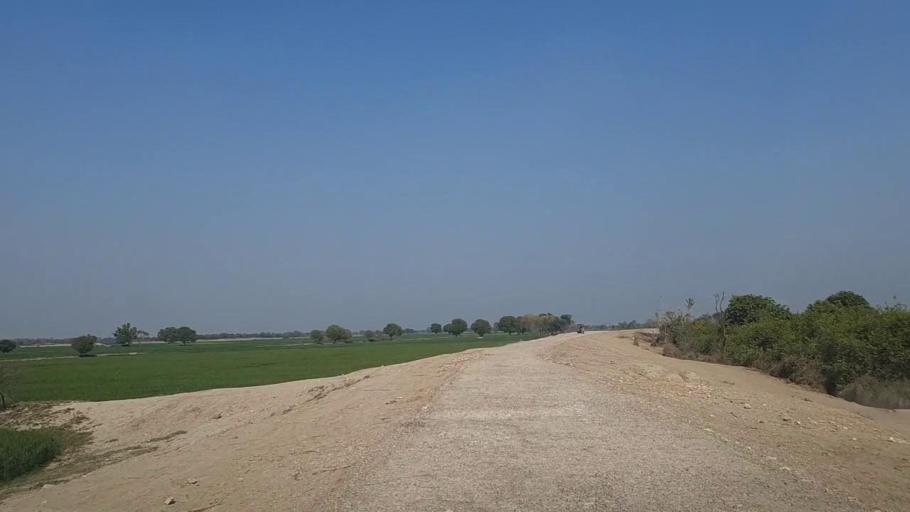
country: PK
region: Sindh
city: Moro
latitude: 26.7949
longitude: 67.9377
